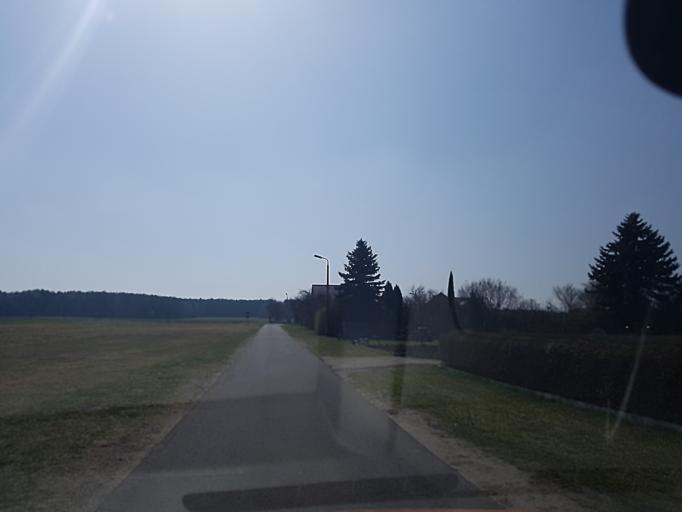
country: DE
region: Saxony
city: Gross Duben
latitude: 51.6657
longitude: 14.5541
